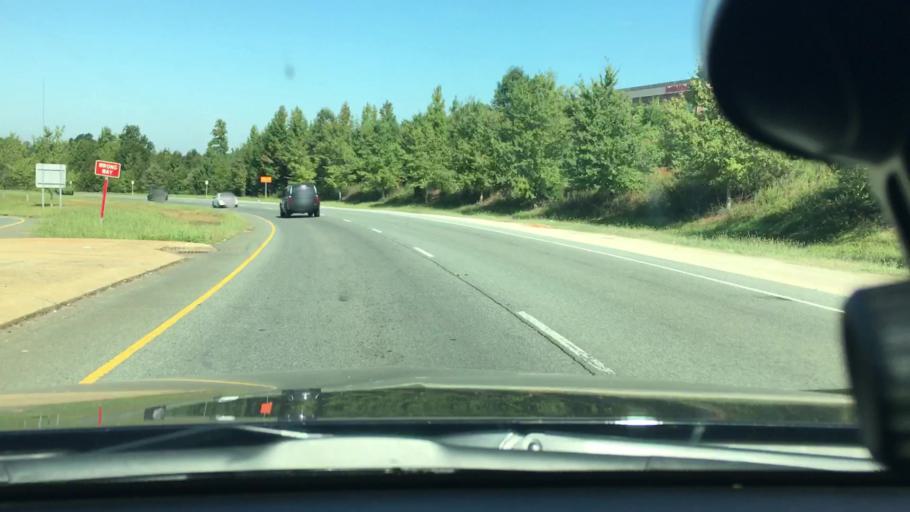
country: US
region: North Carolina
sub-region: Mecklenburg County
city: Mint Hill
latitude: 35.2214
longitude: -80.6480
